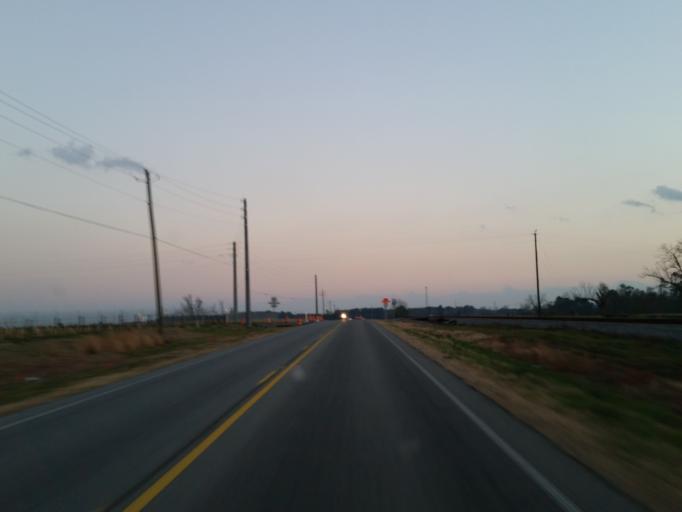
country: US
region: Georgia
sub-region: Tift County
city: Tifton
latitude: 31.5073
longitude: -83.5219
